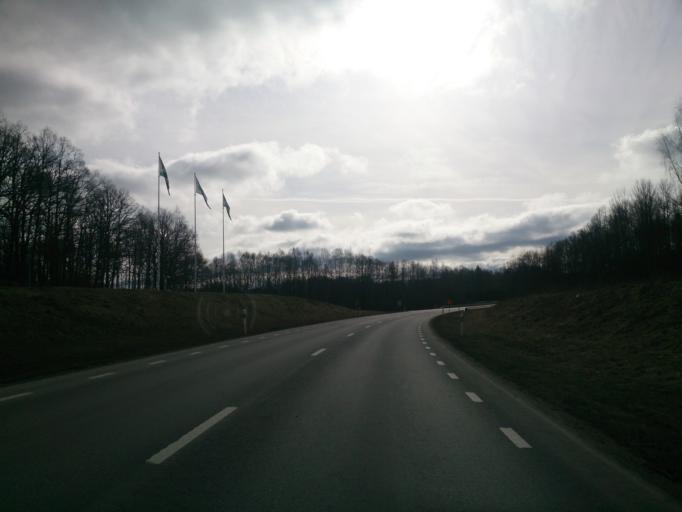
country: SE
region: OEstergoetland
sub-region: Atvidabergs Kommun
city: Atvidaberg
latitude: 58.1956
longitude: 16.0184
